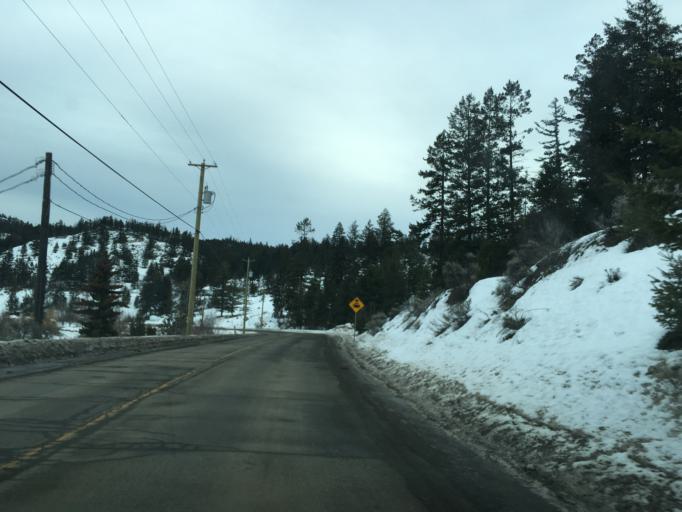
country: CA
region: British Columbia
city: Kamloops
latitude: 50.6557
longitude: -120.4433
